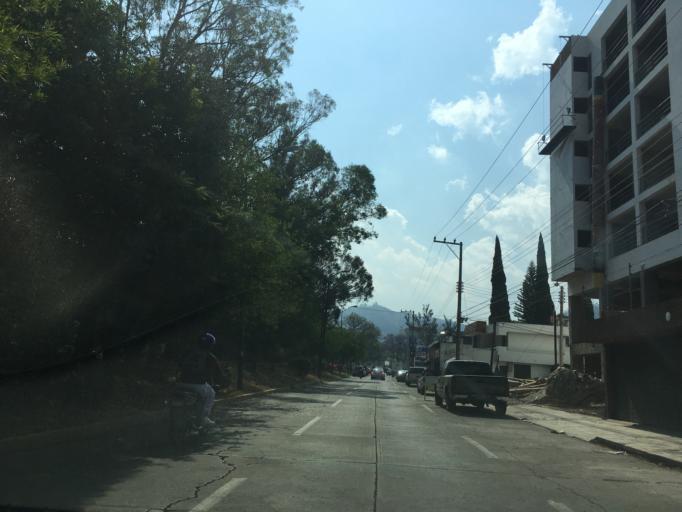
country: MX
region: Michoacan
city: Morelia
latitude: 19.6846
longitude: -101.1678
